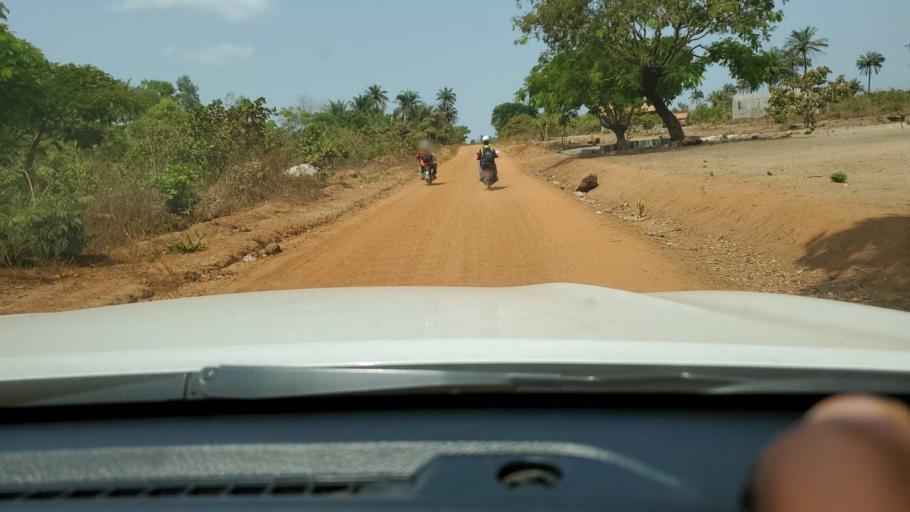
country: GN
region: Boke
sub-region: Boffa
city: Boffa
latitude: 10.0971
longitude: -13.8560
